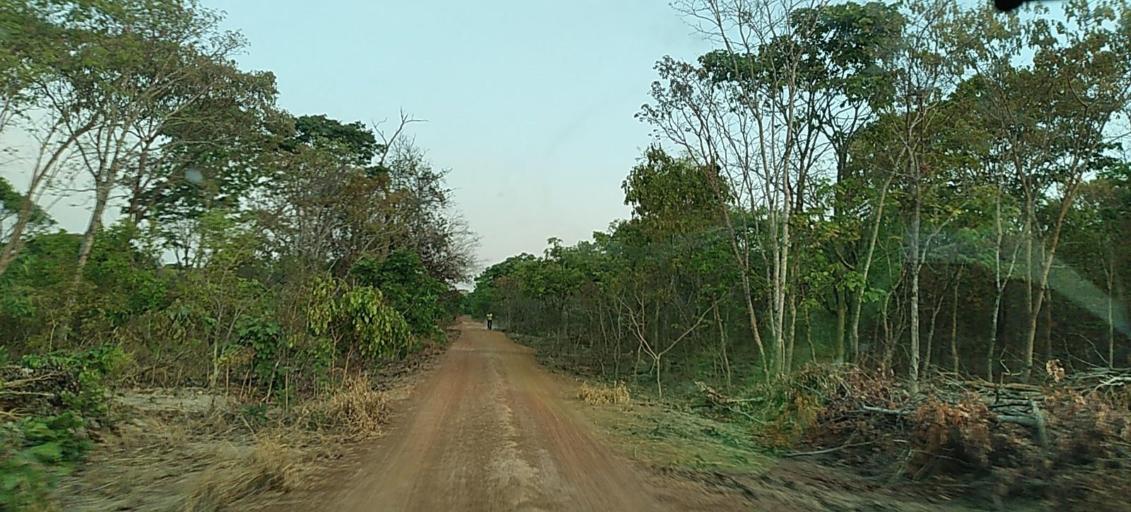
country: ZM
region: North-Western
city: Kalengwa
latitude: -13.1145
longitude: 25.1696
